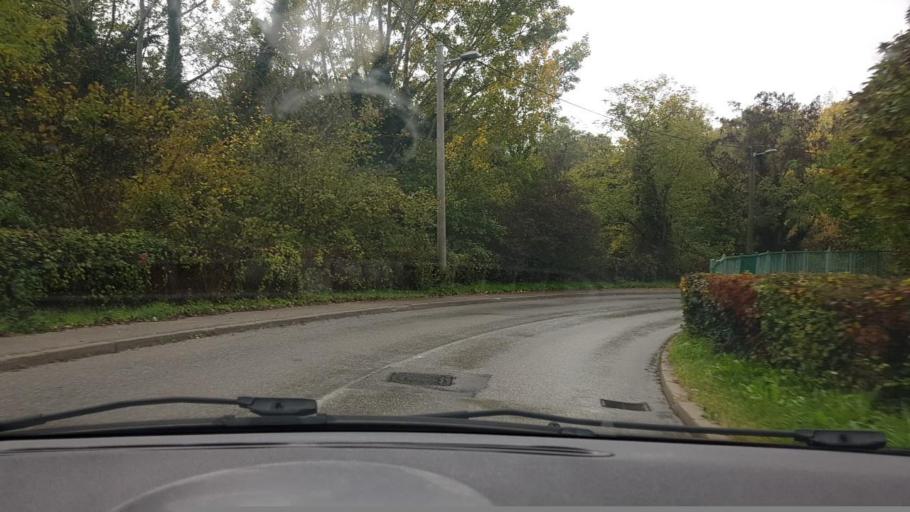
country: HR
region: Grad Zagreb
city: Zagreb
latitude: 45.8478
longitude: 15.9850
